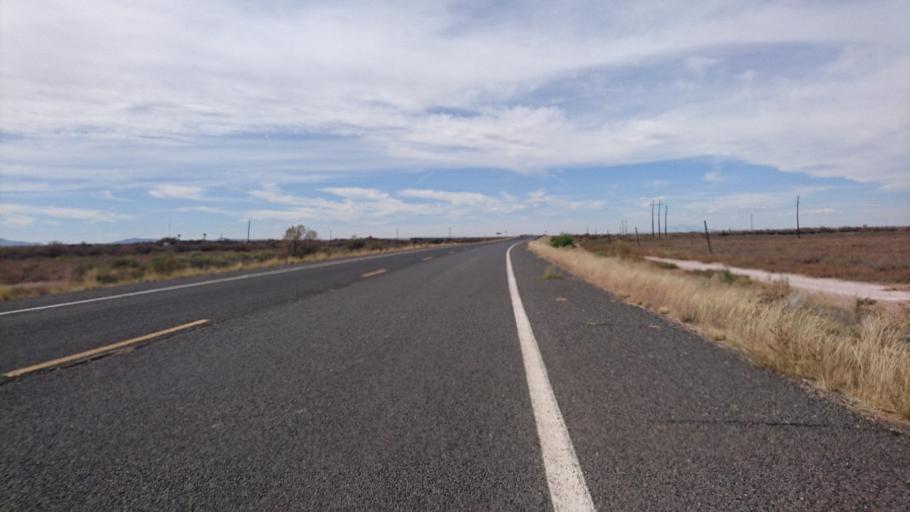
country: US
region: Arizona
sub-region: Navajo County
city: Winslow
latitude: 35.0058
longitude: -110.6467
